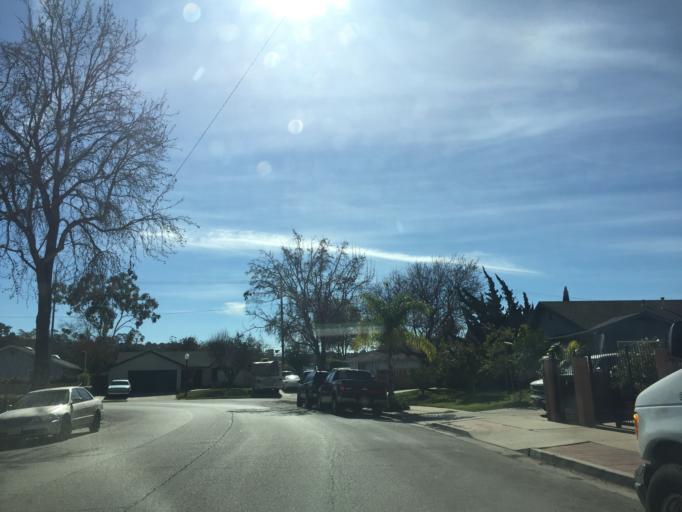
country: US
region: California
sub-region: Santa Barbara County
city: Goleta
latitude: 34.4385
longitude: -119.7846
